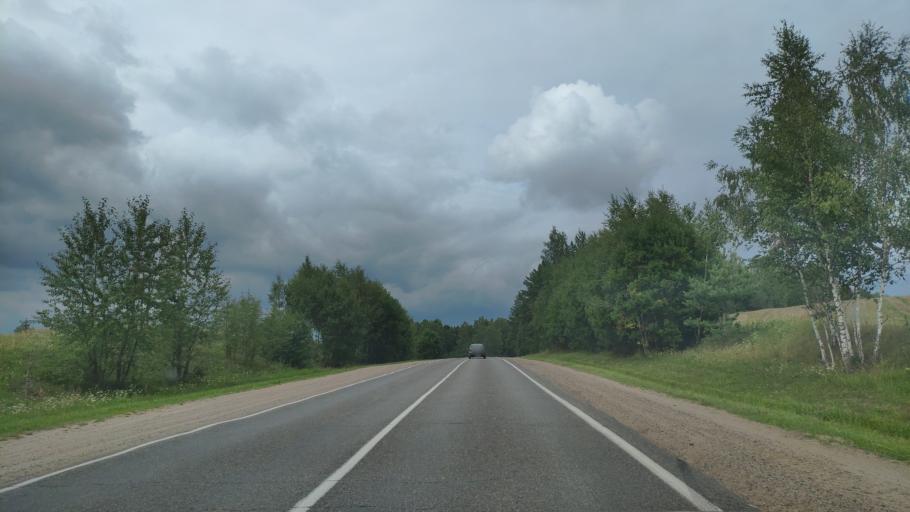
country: BY
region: Minsk
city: Zaslawye
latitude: 53.9627
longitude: 27.2448
